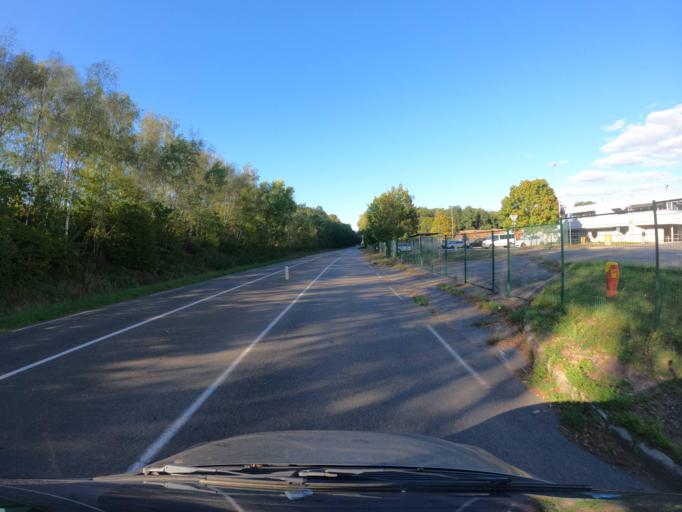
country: FR
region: Bourgogne
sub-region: Departement de Saone-et-Loire
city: Torcy
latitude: 46.7576
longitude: 4.4410
